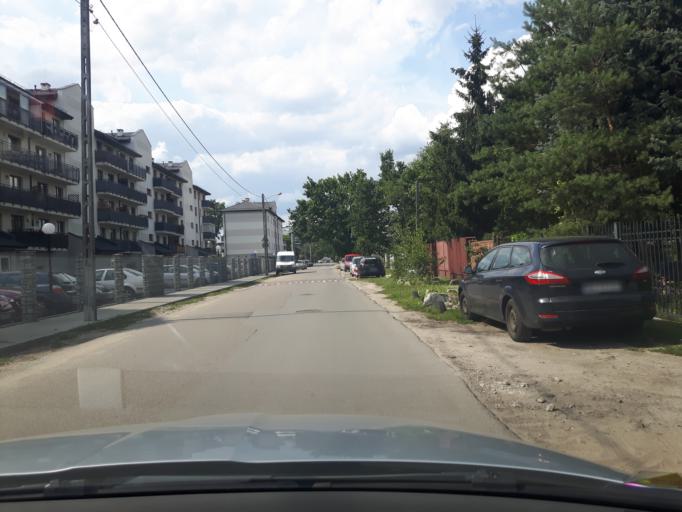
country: PL
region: Masovian Voivodeship
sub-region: Powiat wolominski
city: Marki
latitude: 52.3086
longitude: 21.1020
